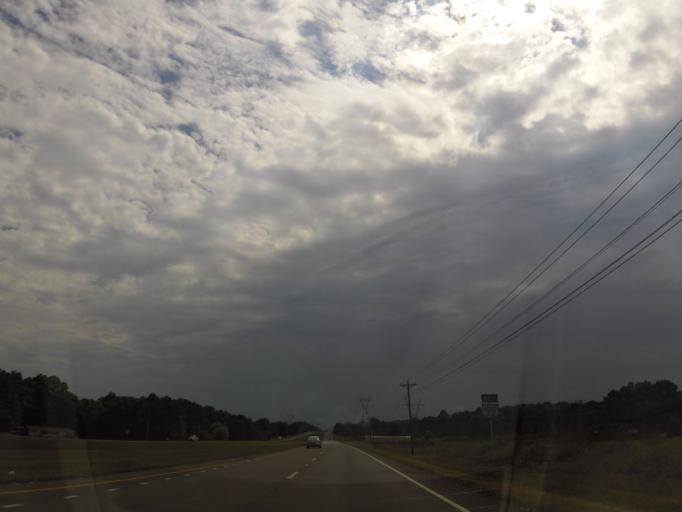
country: US
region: Alabama
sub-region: Jackson County
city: Scottsboro
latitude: 34.7348
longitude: -85.9337
